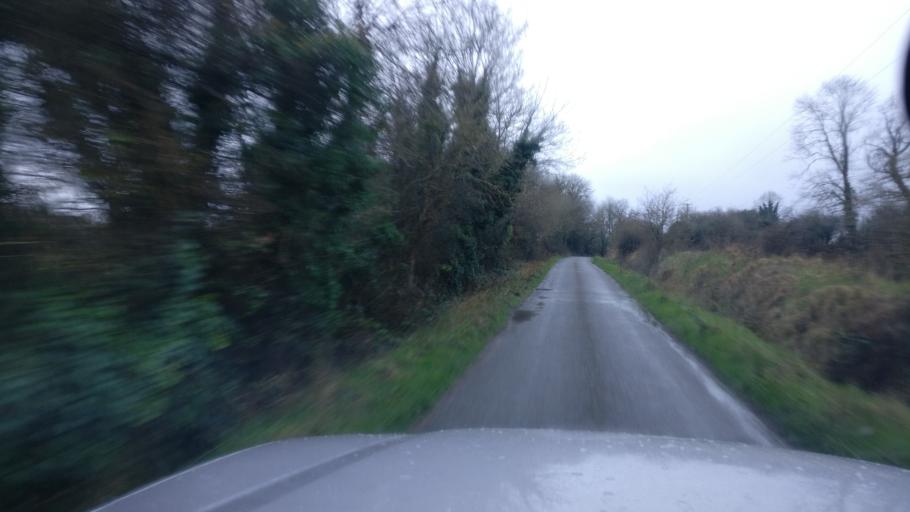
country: IE
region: Connaught
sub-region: County Galway
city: Ballinasloe
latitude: 53.2606
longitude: -8.3790
